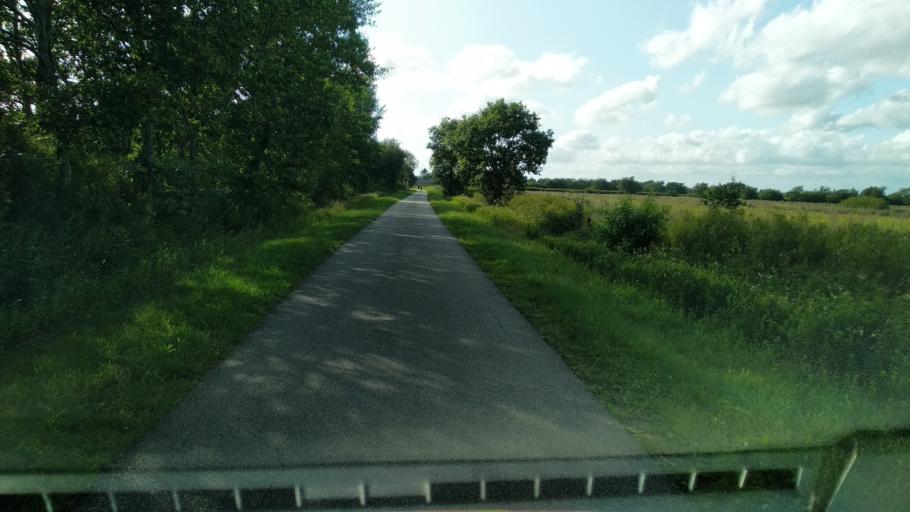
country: DE
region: Schleswig-Holstein
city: Gross Rheide
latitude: 54.4272
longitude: 9.4277
